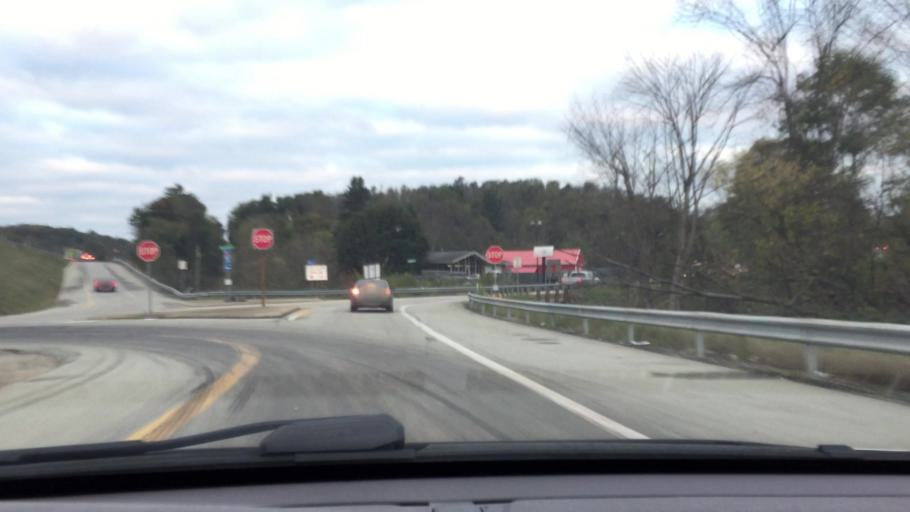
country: US
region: Pennsylvania
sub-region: Washington County
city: Ellsworth
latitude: 40.1671
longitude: -80.0842
